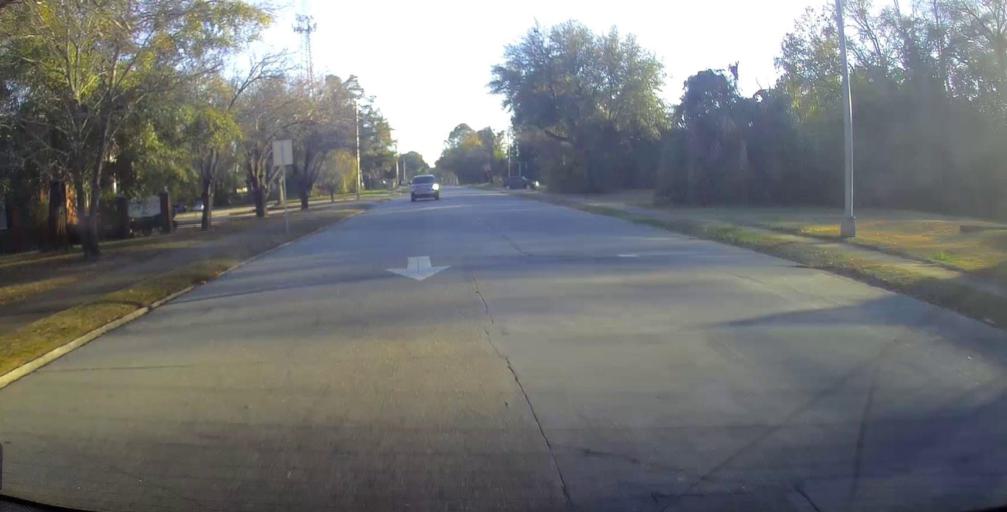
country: US
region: Georgia
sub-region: Dougherty County
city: Albany
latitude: 31.5838
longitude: -84.1591
